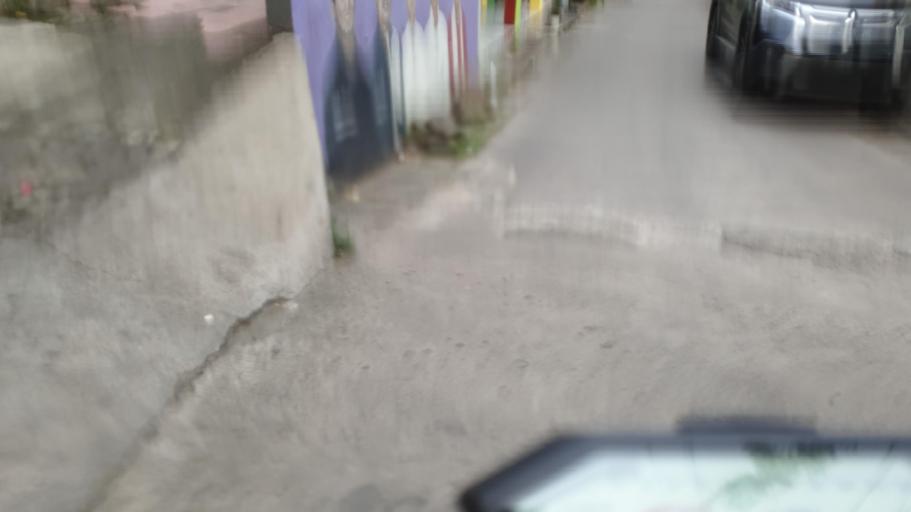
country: ID
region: West Java
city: Depok
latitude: -6.3689
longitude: 106.8375
